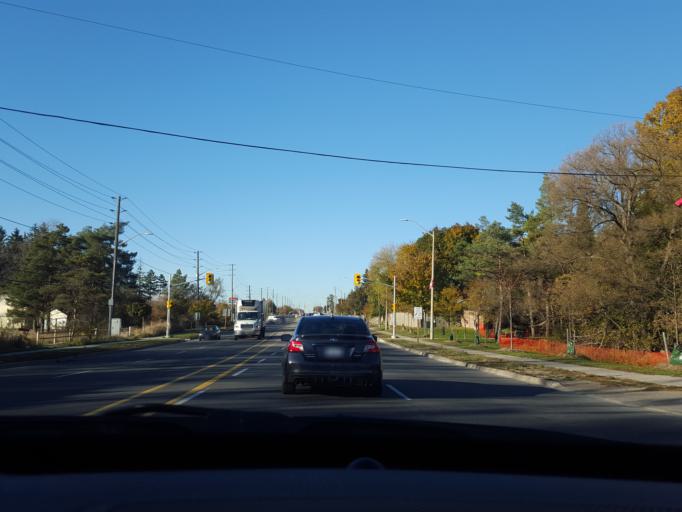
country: CA
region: Ontario
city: Markham
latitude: 43.8630
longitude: -79.2834
